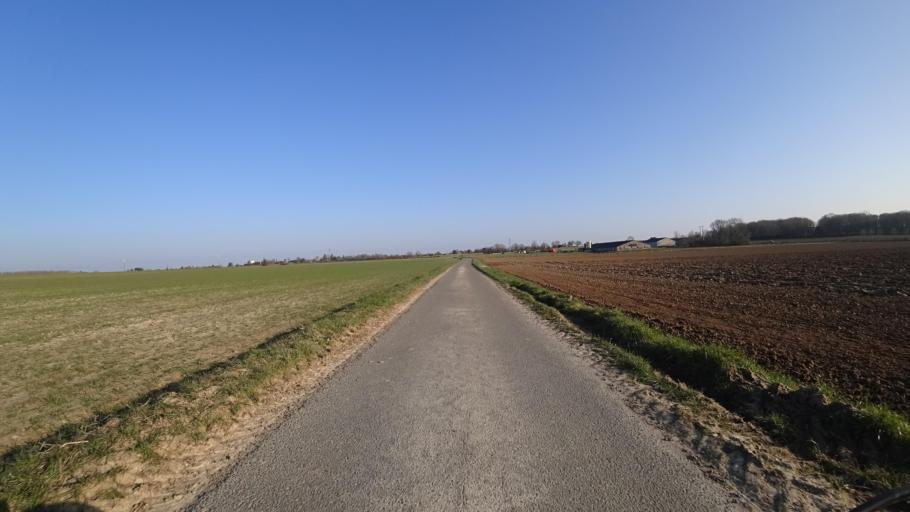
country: BE
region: Wallonia
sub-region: Province de Namur
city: Gembloux
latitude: 50.5707
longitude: 4.6666
